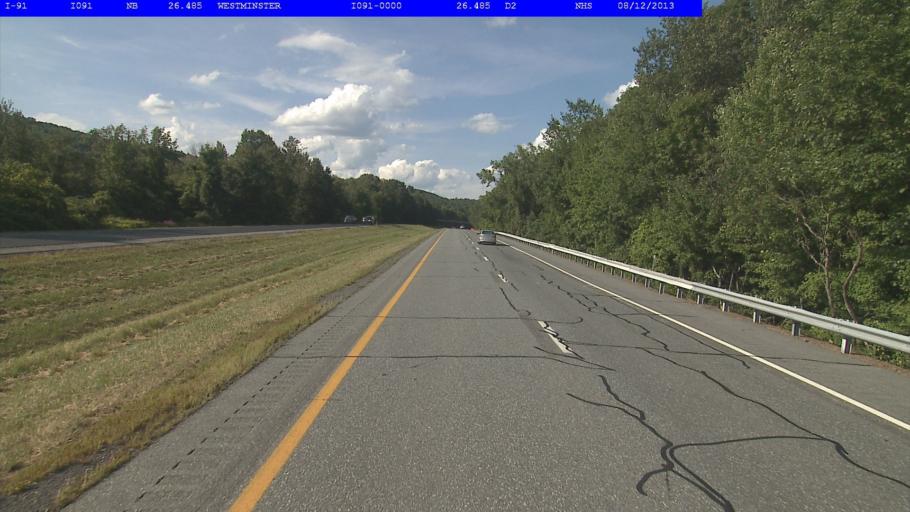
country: US
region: Vermont
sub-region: Windham County
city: Bellows Falls
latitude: 43.0625
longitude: -72.4702
